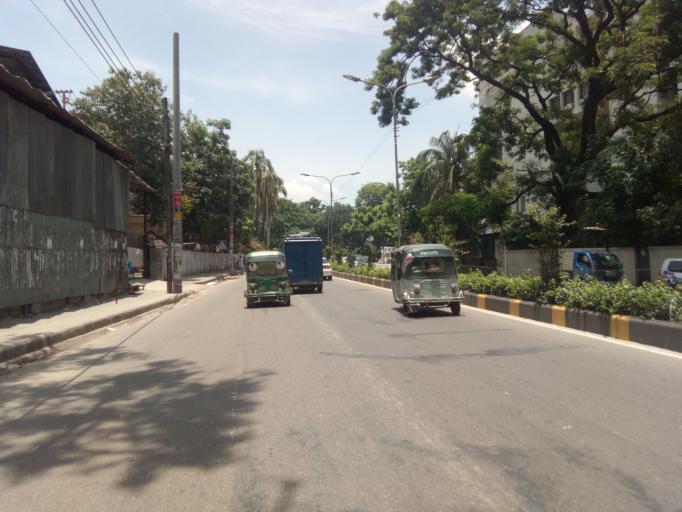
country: BD
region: Dhaka
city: Paltan
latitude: 23.7364
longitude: 90.4038
